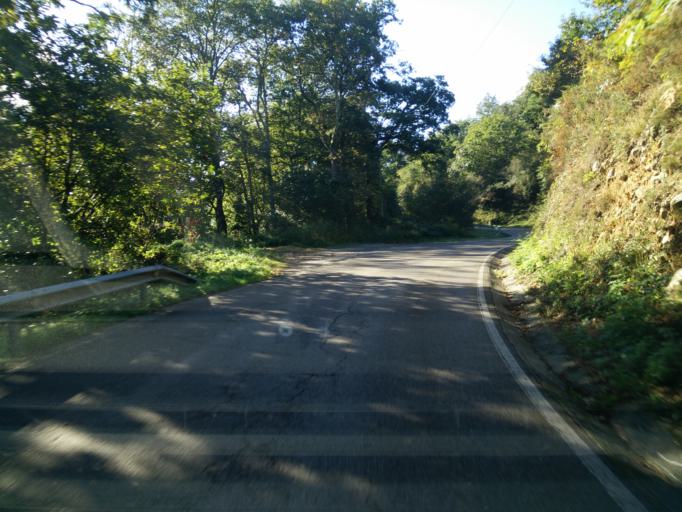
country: ES
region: Cantabria
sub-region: Provincia de Cantabria
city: San Pedro del Romeral
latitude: 43.1464
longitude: -3.8189
